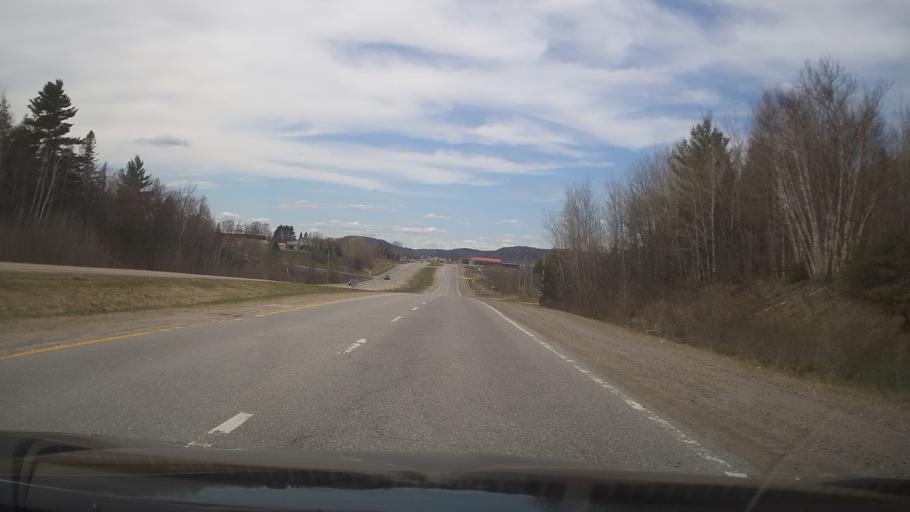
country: CA
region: Quebec
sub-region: Outaouais
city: Wakefield
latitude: 45.5336
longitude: -76.0098
